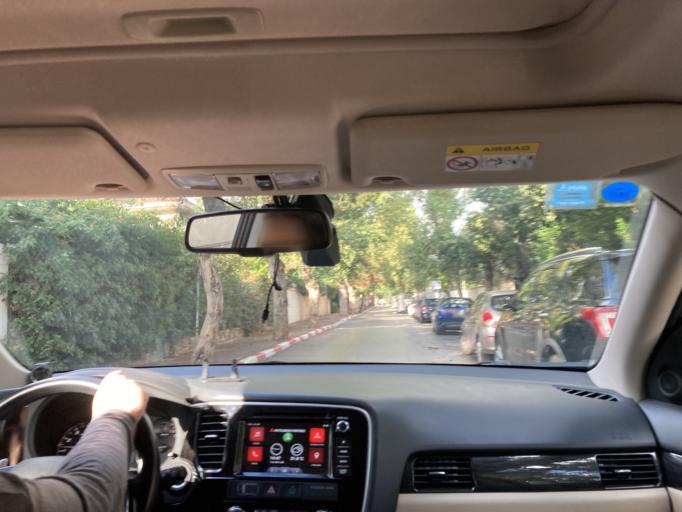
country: IL
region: Tel Aviv
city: Ramat HaSharon
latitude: 32.1508
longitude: 34.8344
